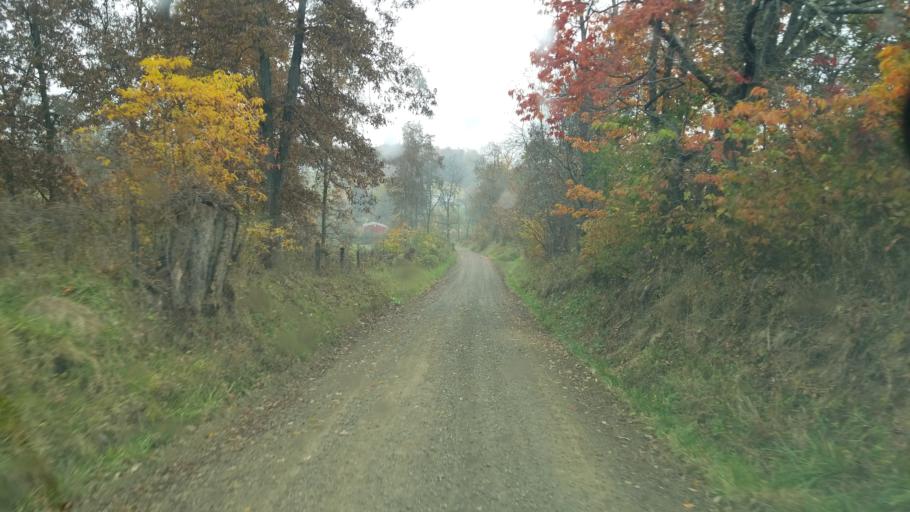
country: US
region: Ohio
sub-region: Holmes County
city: Millersburg
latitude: 40.4228
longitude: -81.8634
